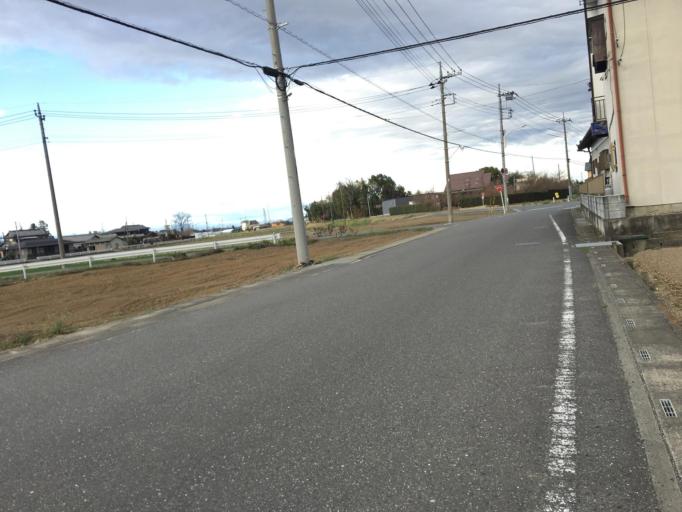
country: JP
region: Saitama
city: Yorii
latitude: 36.1233
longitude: 139.2623
